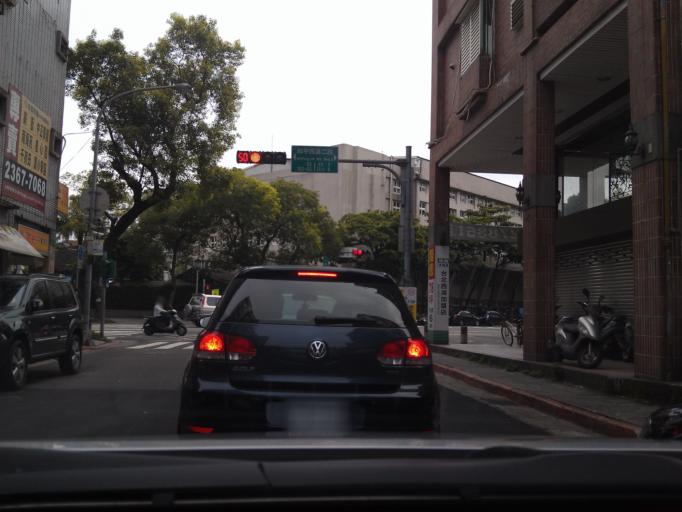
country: TW
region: Taipei
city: Taipei
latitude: 25.0287
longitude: 121.5118
